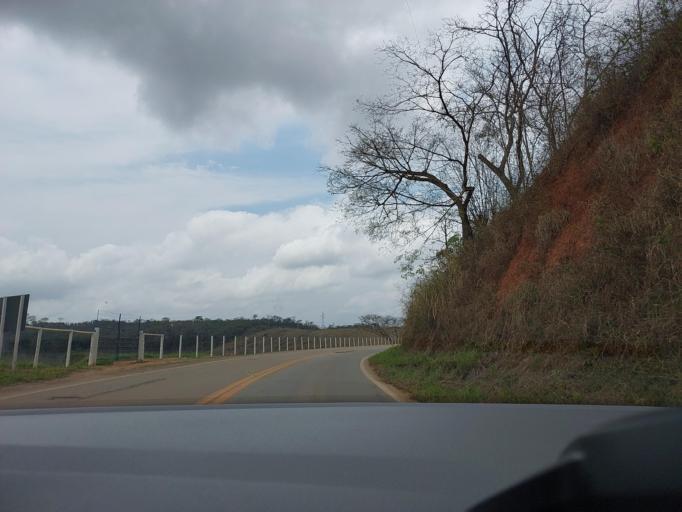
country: BR
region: Minas Gerais
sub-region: Ponte Nova
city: Ponte Nova
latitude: -20.3852
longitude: -42.8719
